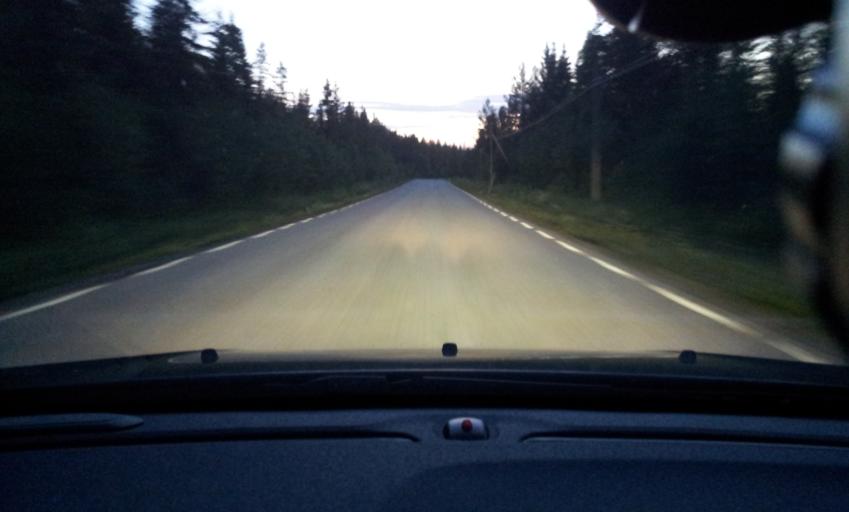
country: SE
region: Jaemtland
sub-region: Bergs Kommun
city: Hoverberg
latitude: 62.7531
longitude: 14.5692
